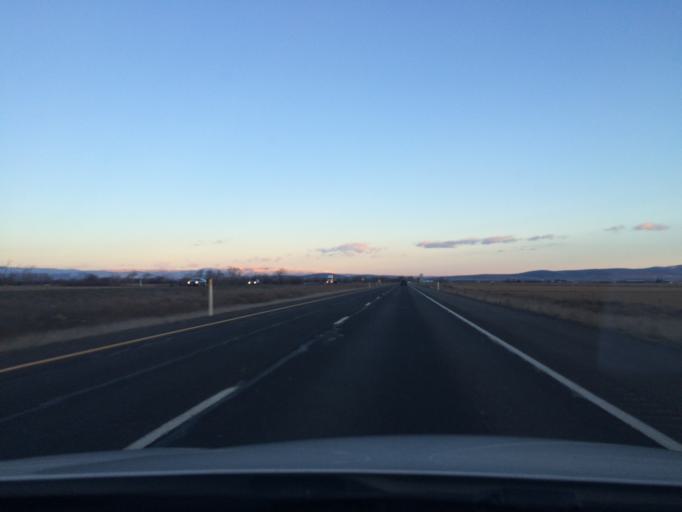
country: US
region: Washington
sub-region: Kittitas County
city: Ellensburg
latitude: 46.9705
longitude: -120.4939
